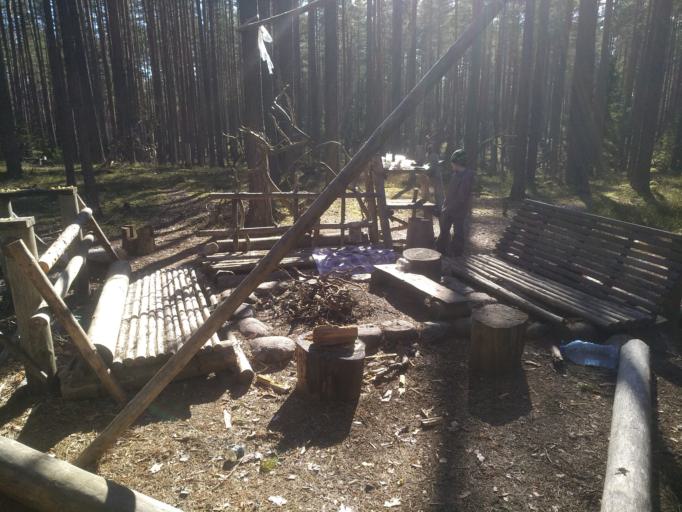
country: RU
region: Leningrad
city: Sapernoye
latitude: 60.6230
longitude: 30.0438
